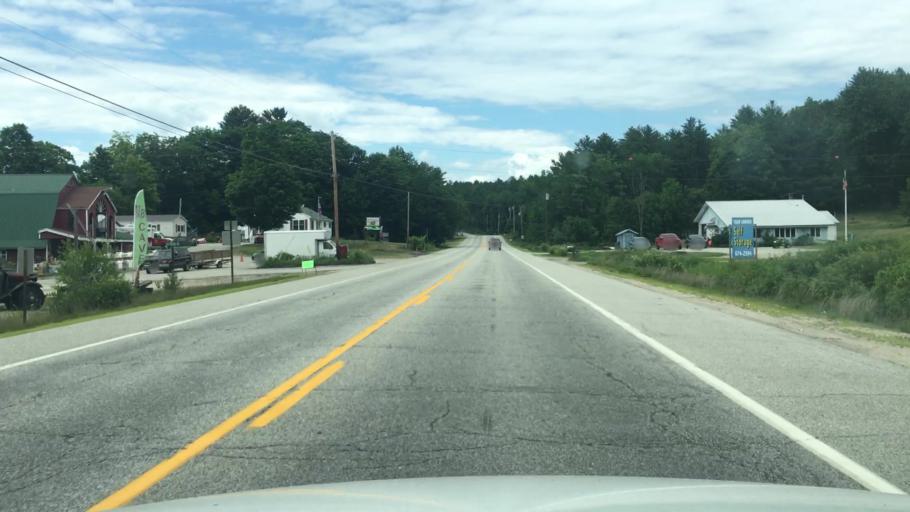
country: US
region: Maine
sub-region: Oxford County
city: West Paris
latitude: 44.3340
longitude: -70.5558
